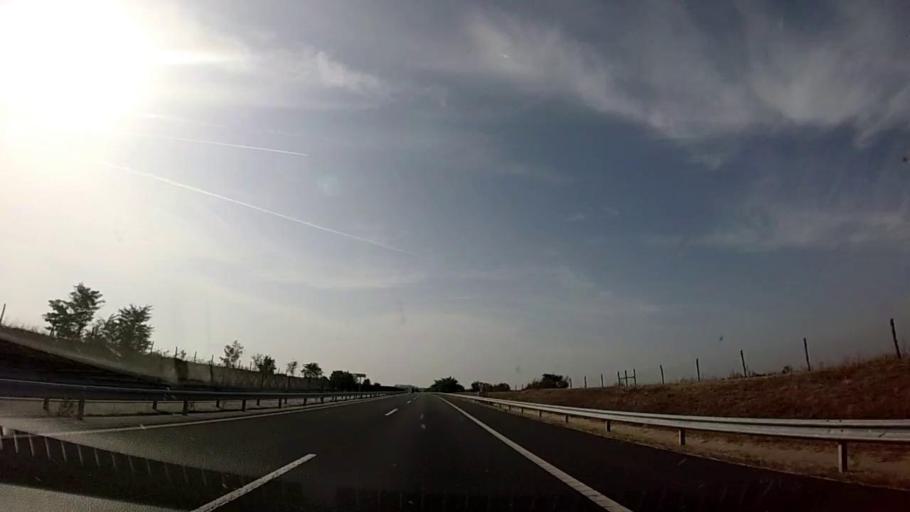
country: HU
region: Zala
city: Zalakomar
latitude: 46.6129
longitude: 17.2577
